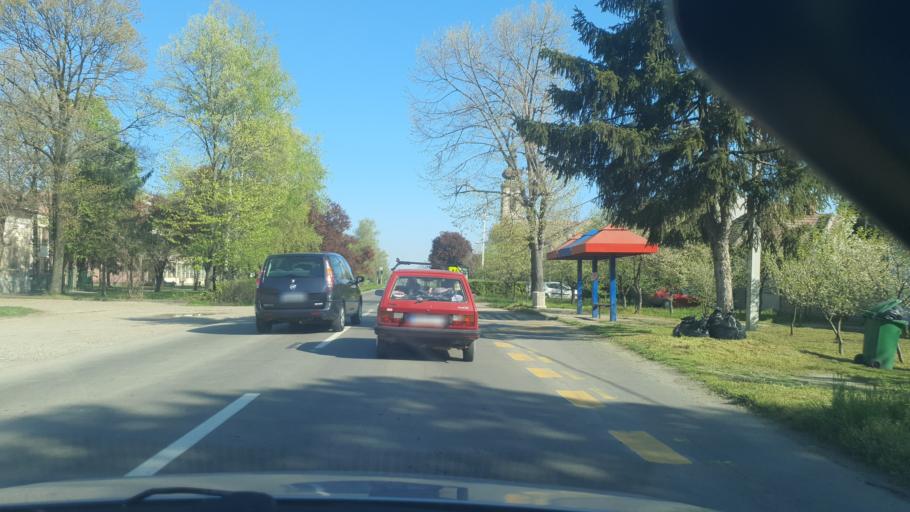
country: RS
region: Autonomna Pokrajina Vojvodina
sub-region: Zapadnobacki Okrug
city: Kula
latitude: 45.7103
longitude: 19.3797
